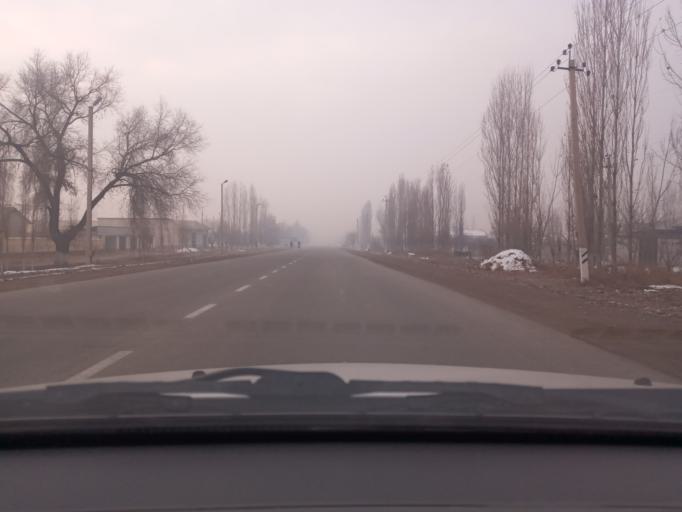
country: UZ
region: Namangan
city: Pop
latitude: 40.8890
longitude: 71.1472
